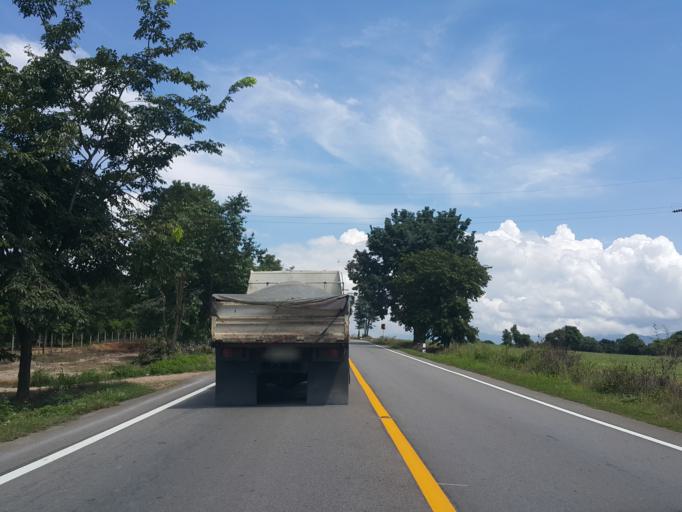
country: TH
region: Chiang Mai
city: Phrao
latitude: 19.2615
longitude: 99.1882
